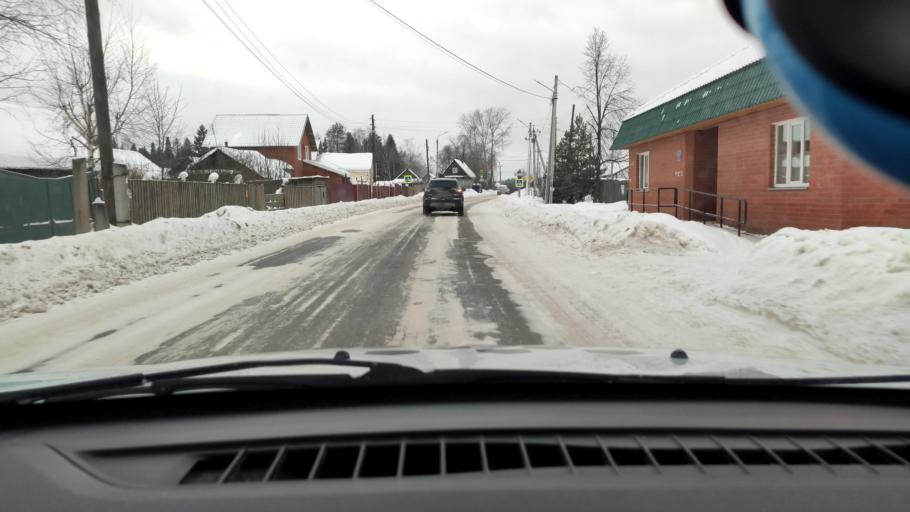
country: RU
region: Perm
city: Overyata
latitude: 58.0786
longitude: 55.9719
